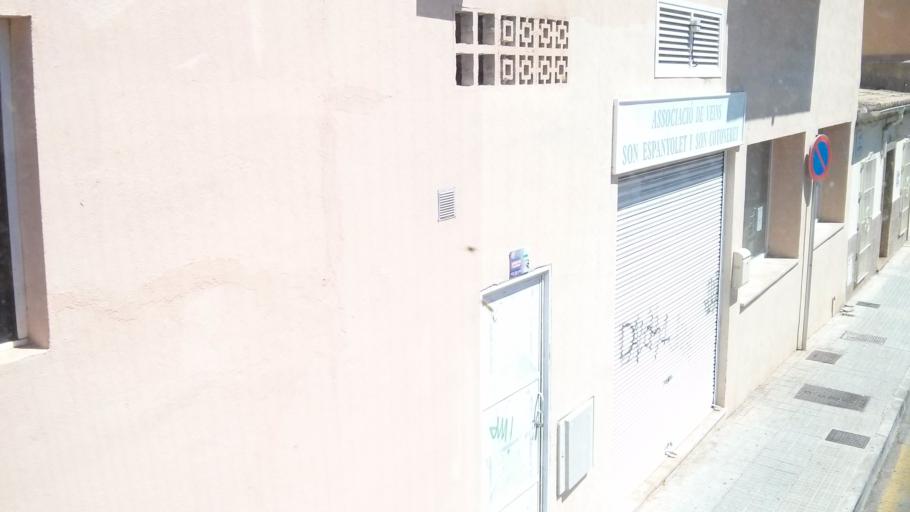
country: ES
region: Balearic Islands
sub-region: Illes Balears
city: Palma
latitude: 39.5731
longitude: 2.6288
